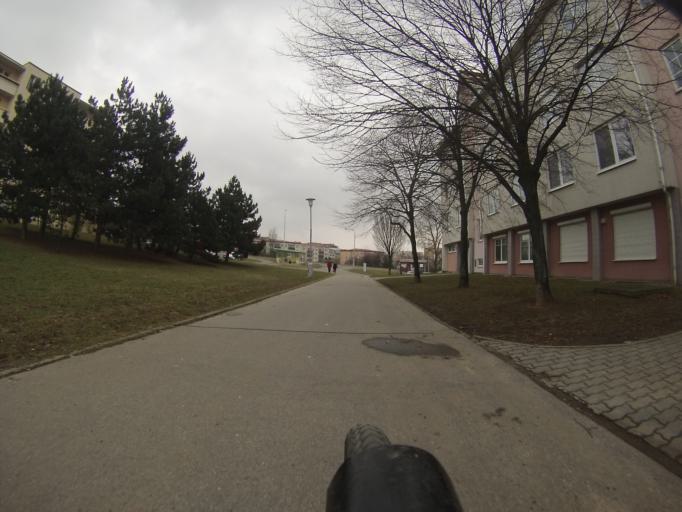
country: CZ
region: South Moravian
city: Bilovice nad Svitavou
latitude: 49.2045
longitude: 16.6777
